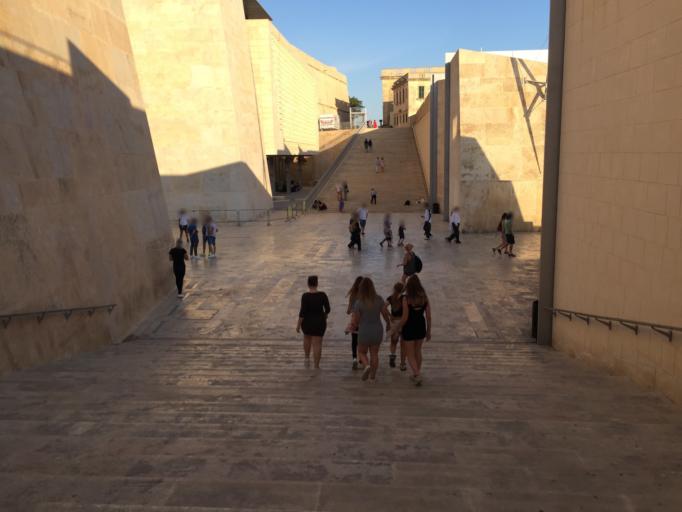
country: MT
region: Il-Furjana
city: Floriana
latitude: 35.8965
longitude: 14.5091
